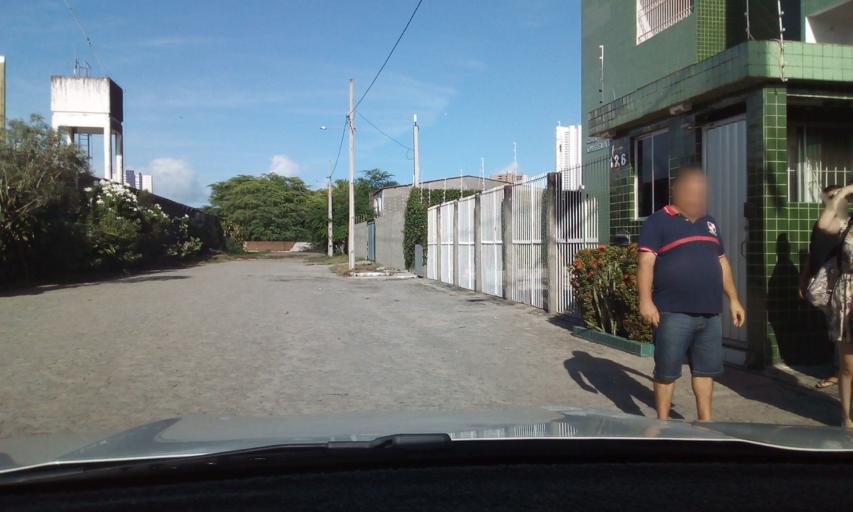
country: BR
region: Paraiba
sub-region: Joao Pessoa
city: Joao Pessoa
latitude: -7.0795
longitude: -34.8483
